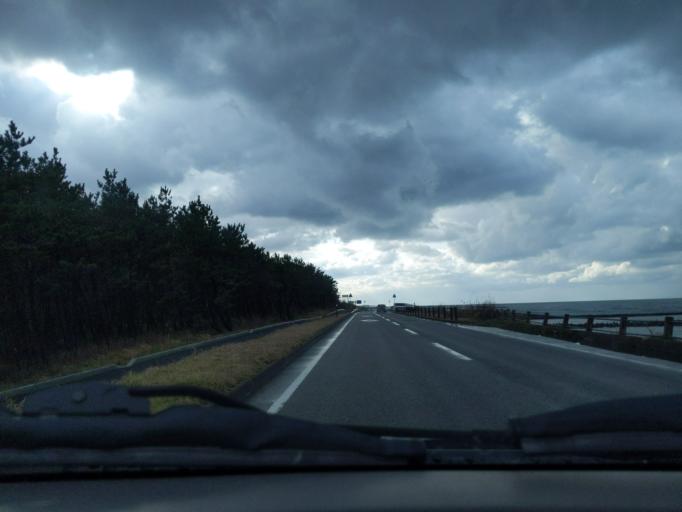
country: JP
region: Niigata
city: Niigata-shi
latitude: 37.9281
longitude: 139.0335
